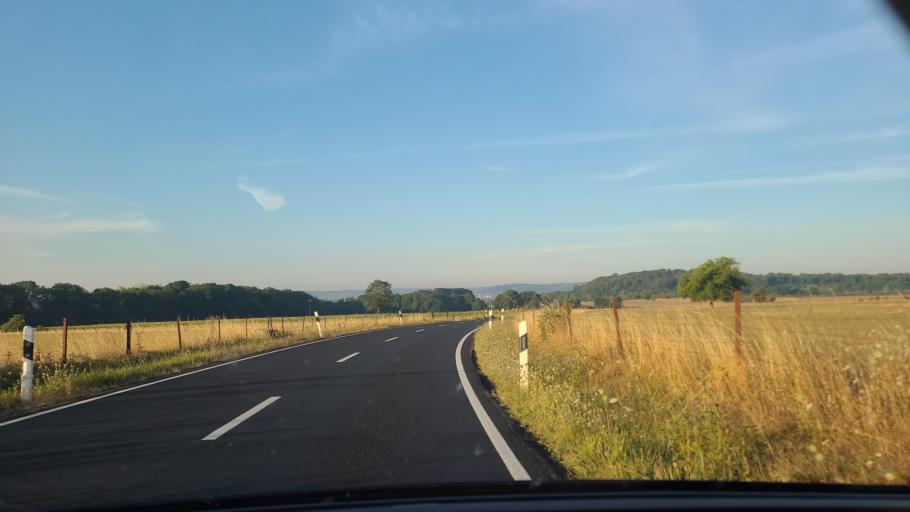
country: LU
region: Luxembourg
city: Hautcharage
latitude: 49.6017
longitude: 5.9168
